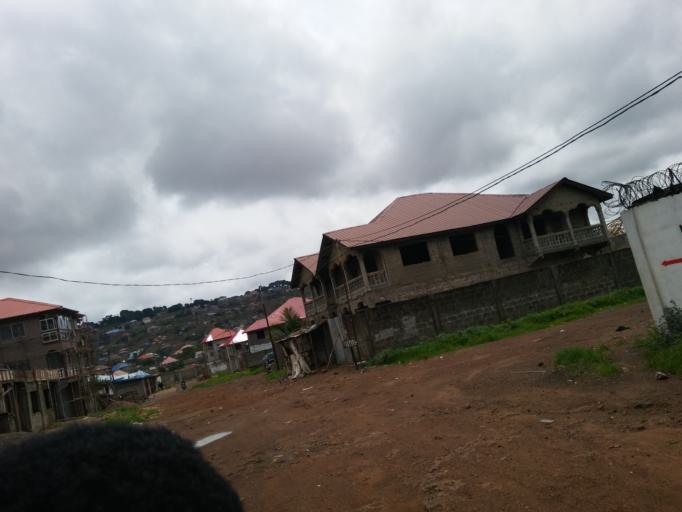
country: SL
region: Western Area
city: Hastings
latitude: 8.4024
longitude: -13.1657
